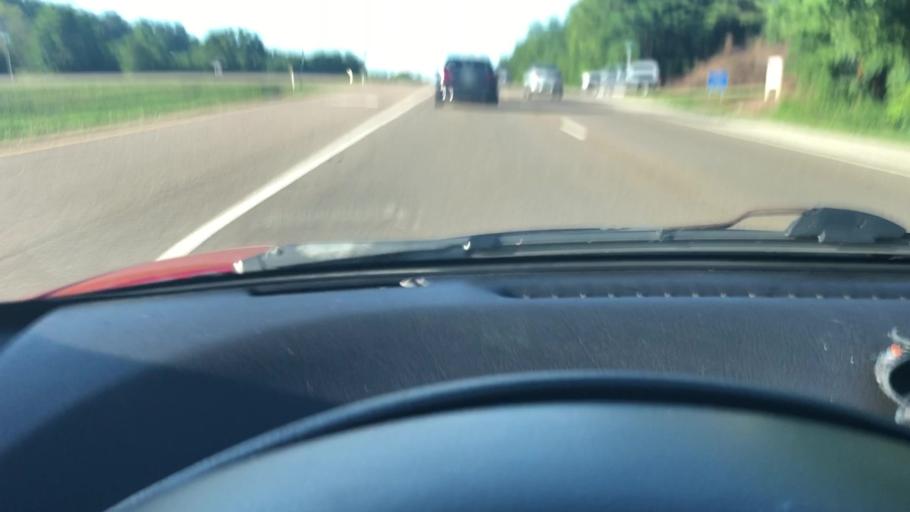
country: US
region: Tennessee
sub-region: Jefferson County
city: Jefferson City
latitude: 36.0675
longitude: -83.4789
